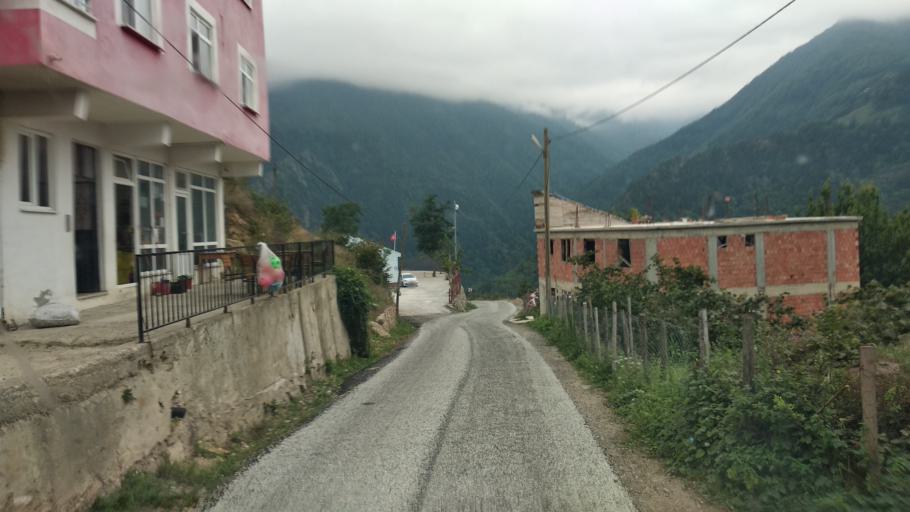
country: TR
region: Giresun
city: Dogankent
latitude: 40.7441
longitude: 38.9913
